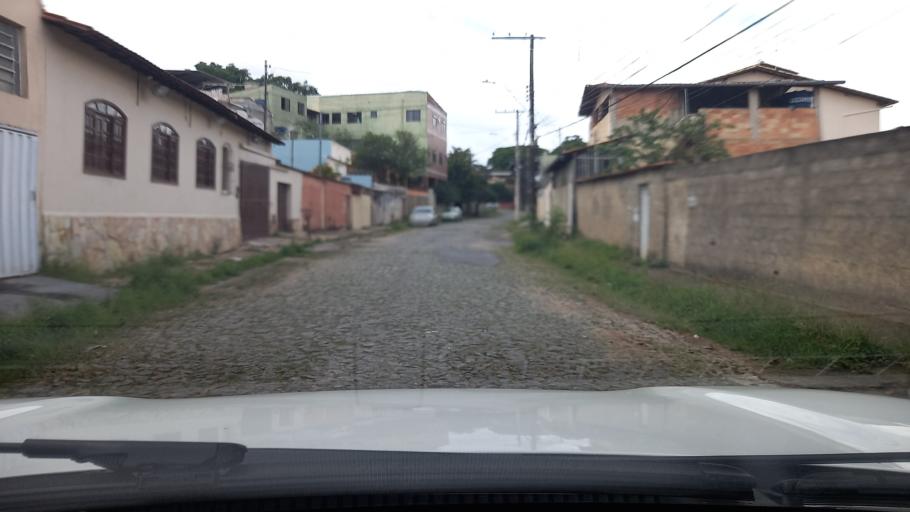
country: BR
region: Minas Gerais
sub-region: Contagem
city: Contagem
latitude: -19.9021
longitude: -44.0056
